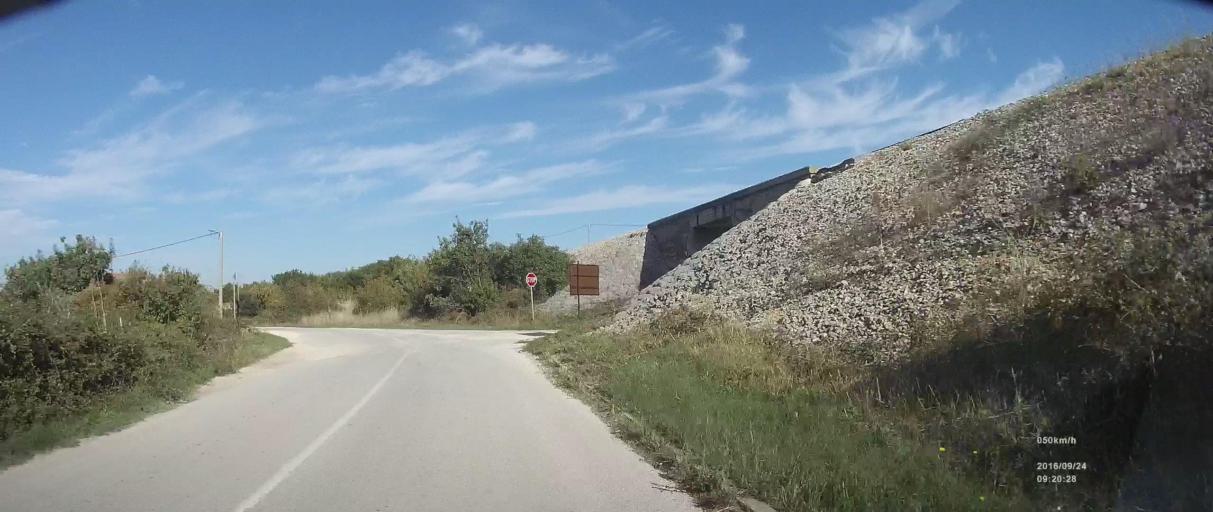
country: HR
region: Zadarska
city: Polaca
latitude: 44.0687
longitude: 15.4969
